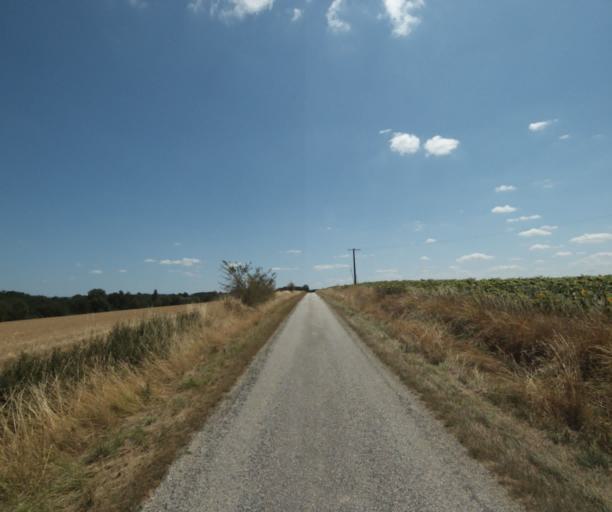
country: FR
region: Midi-Pyrenees
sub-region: Departement de la Haute-Garonne
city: Auriac-sur-Vendinelle
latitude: 43.4967
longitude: 1.8532
